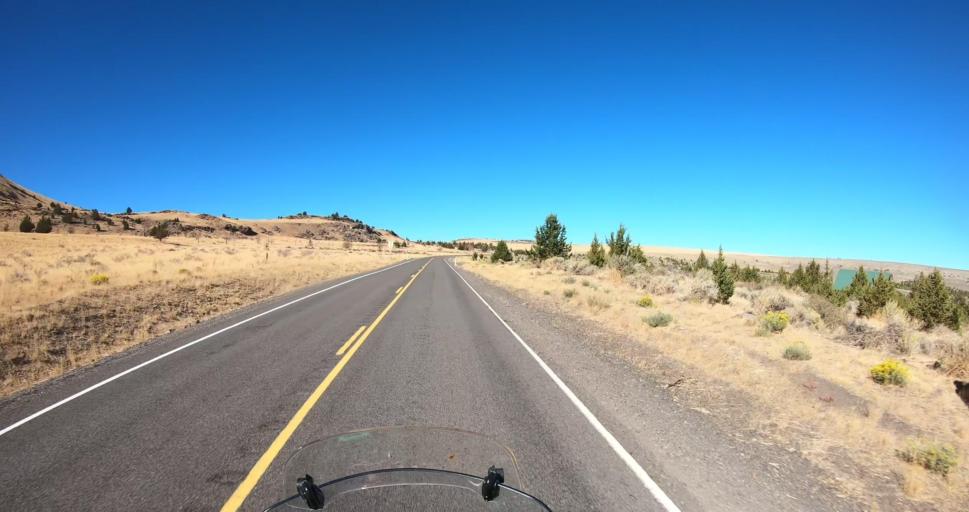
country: US
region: Oregon
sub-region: Lake County
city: Lakeview
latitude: 43.0029
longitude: -120.7761
